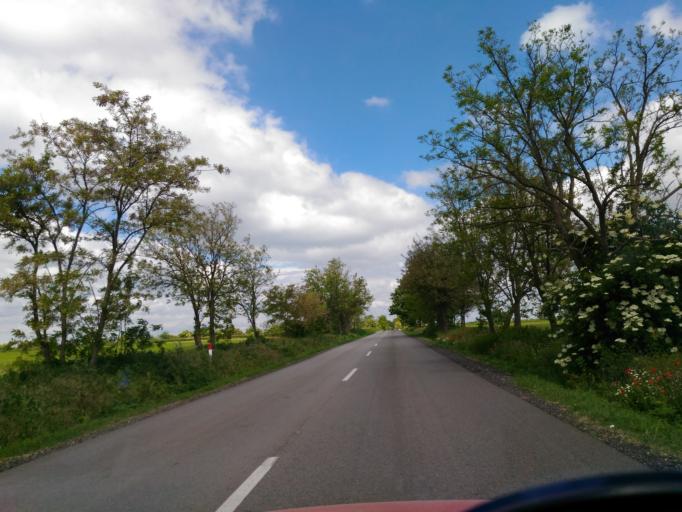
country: HU
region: Fejer
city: Pusztaszabolcs
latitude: 47.1583
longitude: 18.7369
